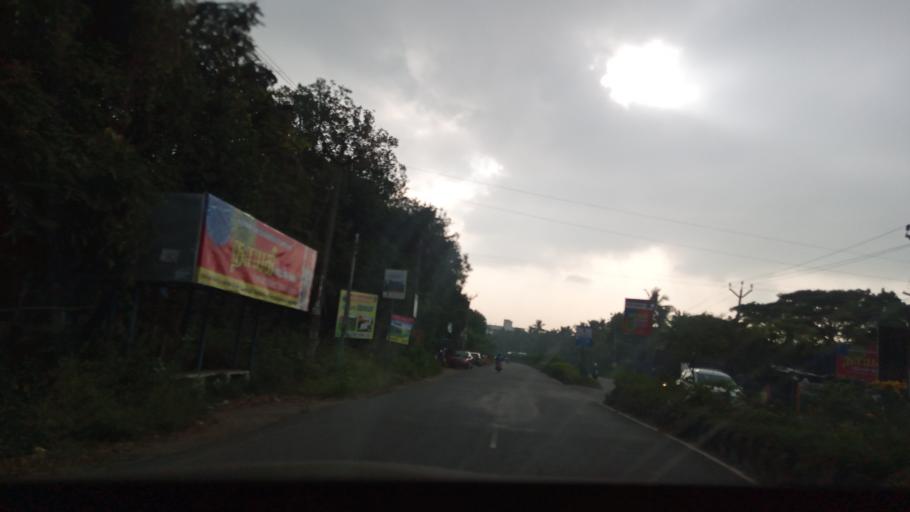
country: IN
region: Tamil Nadu
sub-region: Kancheepuram
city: Vengavasal
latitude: 12.7946
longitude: 80.2088
